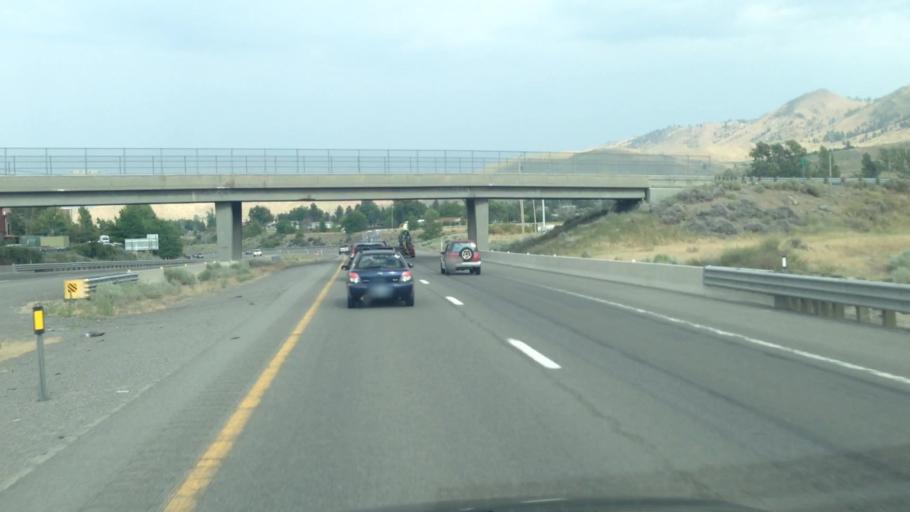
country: US
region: Nevada
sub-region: Washoe County
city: Verdi
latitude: 39.5109
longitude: -119.9650
